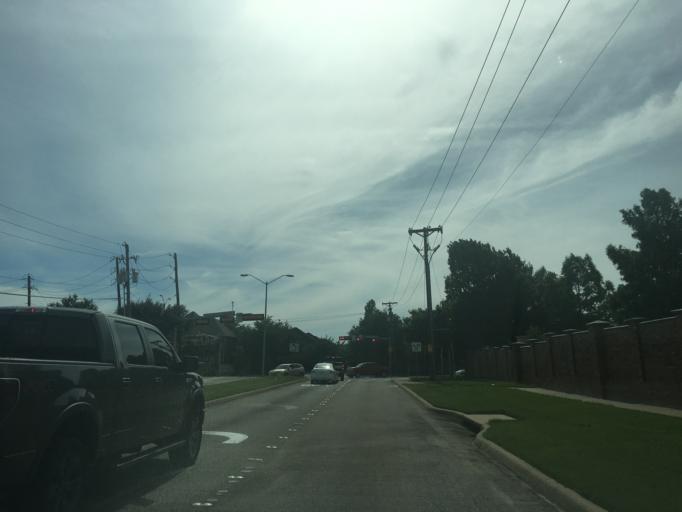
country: US
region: Texas
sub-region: Dallas County
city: Richardson
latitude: 32.9314
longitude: -96.7172
